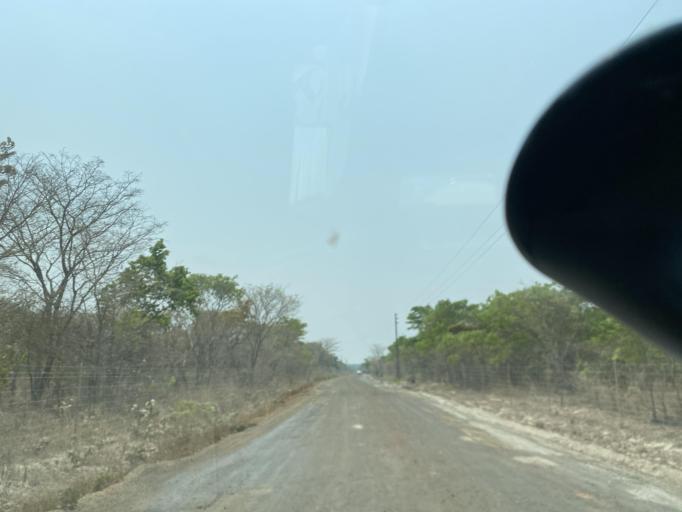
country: ZM
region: Lusaka
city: Lusaka
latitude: -15.5203
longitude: 28.4441
